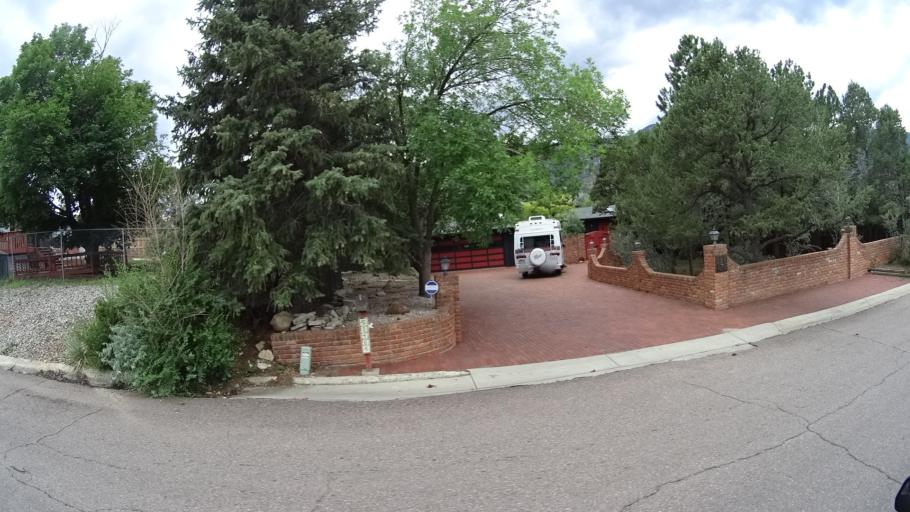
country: US
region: Colorado
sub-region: El Paso County
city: Manitou Springs
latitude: 38.8526
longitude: -104.8900
